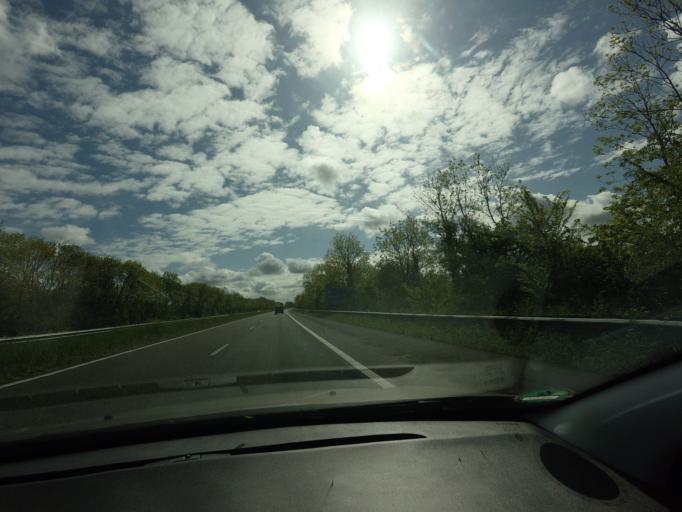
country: NL
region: Friesland
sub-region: Sudwest Fryslan
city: Bolsward
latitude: 53.0576
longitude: 5.5243
